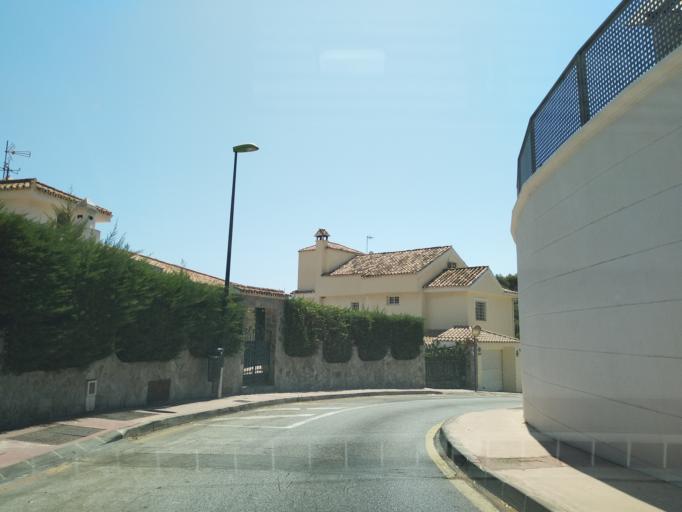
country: ES
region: Andalusia
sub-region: Provincia de Malaga
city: Malaga
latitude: 36.7306
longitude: -4.3799
